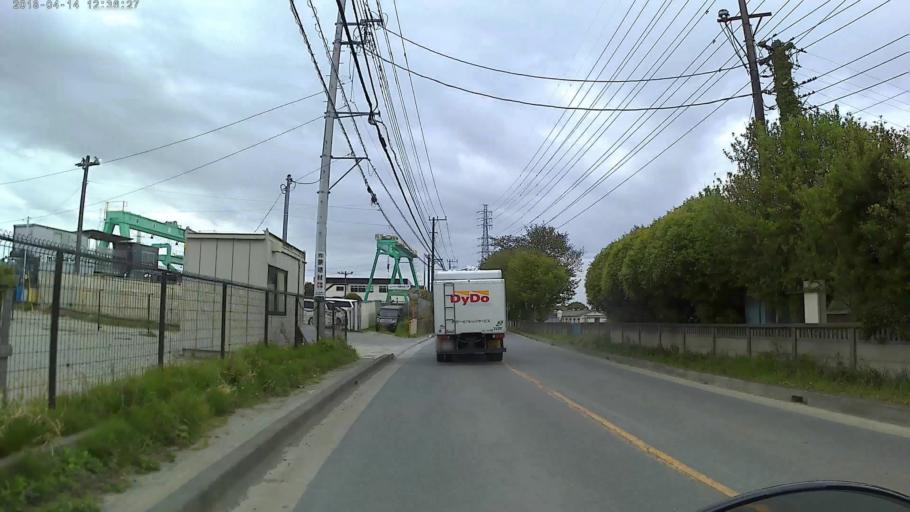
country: JP
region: Kanagawa
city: Atsugi
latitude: 35.4160
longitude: 139.4076
